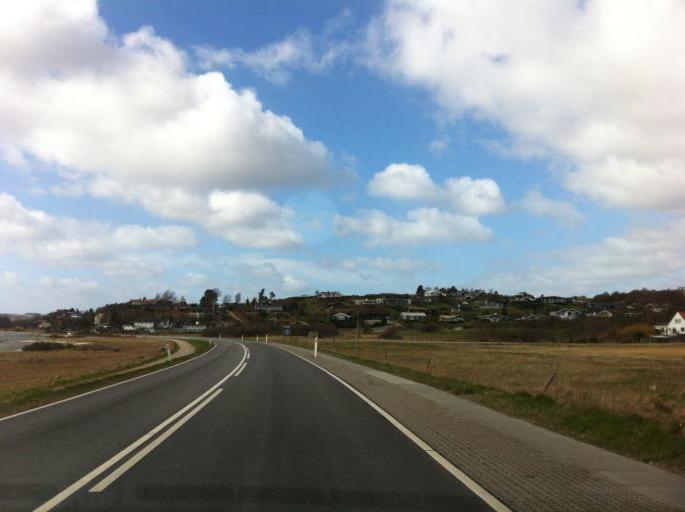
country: DK
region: Central Jutland
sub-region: Syddjurs Kommune
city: Ebeltoft
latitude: 56.2265
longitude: 10.6458
